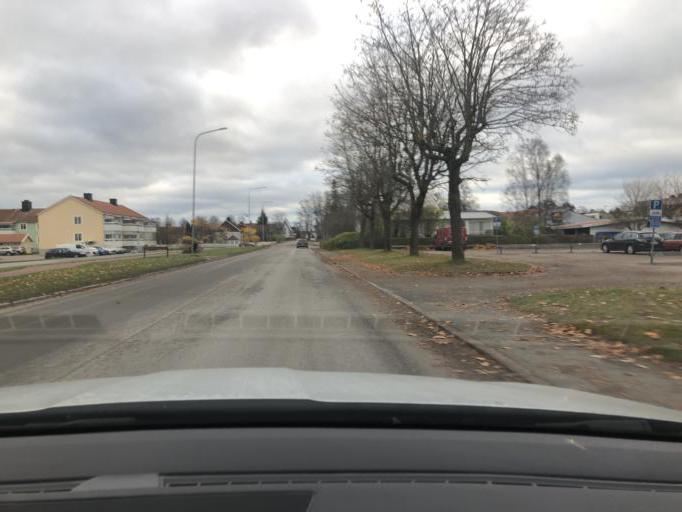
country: SE
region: Uppsala
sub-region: Tierps Kommun
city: Tierp
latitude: 60.3443
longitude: 17.5070
